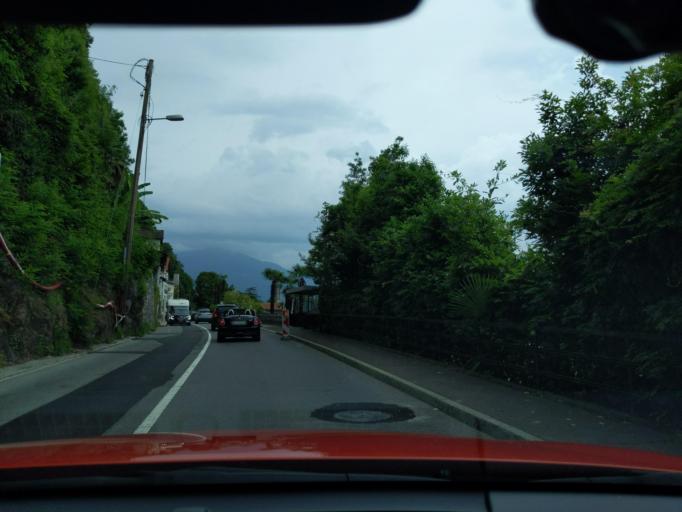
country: CH
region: Ticino
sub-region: Locarno District
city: Brissago
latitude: 46.1084
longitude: 8.7009
